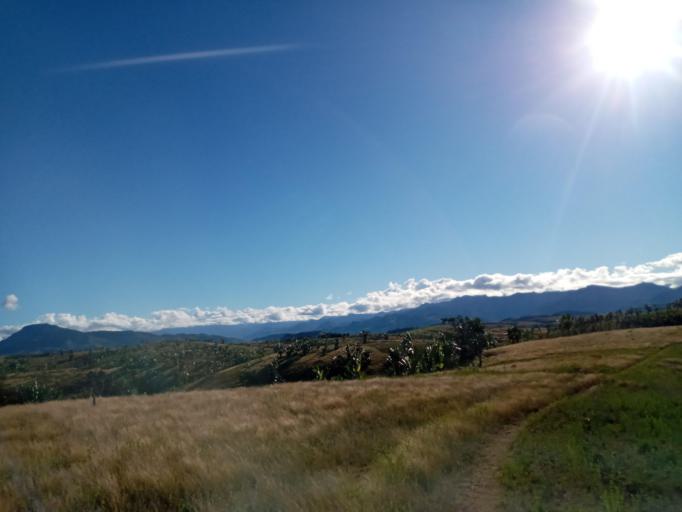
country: MG
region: Anosy
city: Fort Dauphin
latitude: -24.4066
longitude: 47.2514
